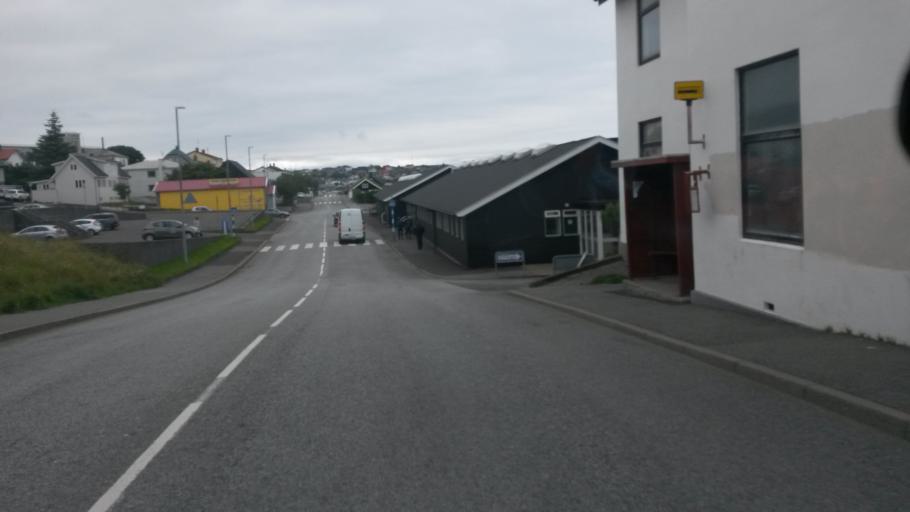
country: FO
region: Streymoy
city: Argir
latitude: 62.0027
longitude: -6.7777
